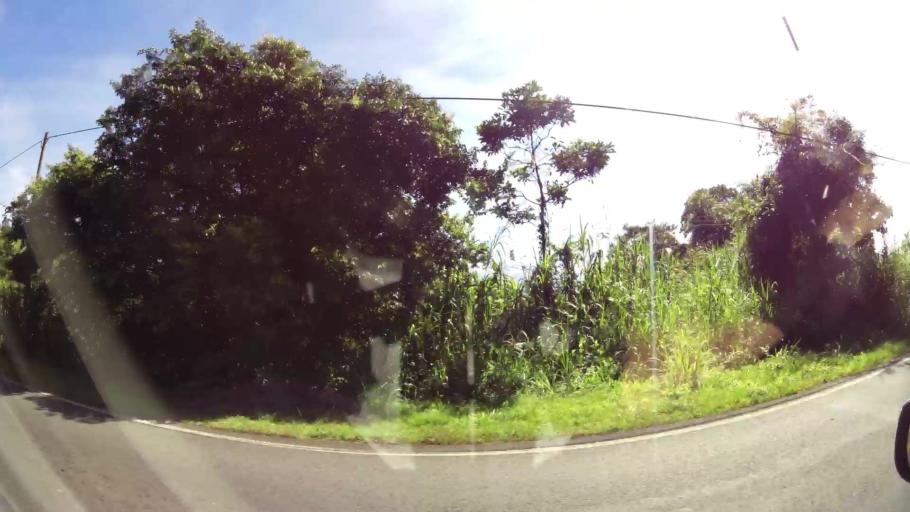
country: CR
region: San Jose
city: San Isidro
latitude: 9.4277
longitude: -83.7116
